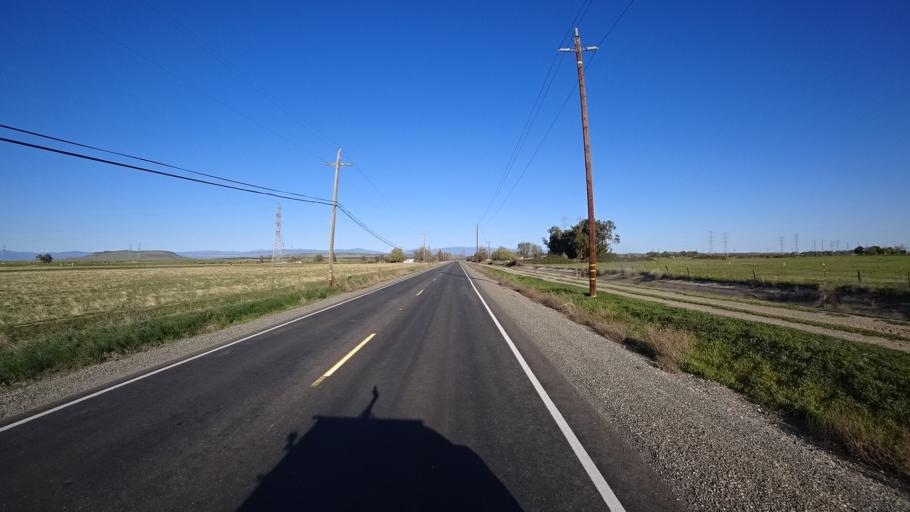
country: US
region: California
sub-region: Glenn County
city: Orland
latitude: 39.7716
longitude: -122.2626
